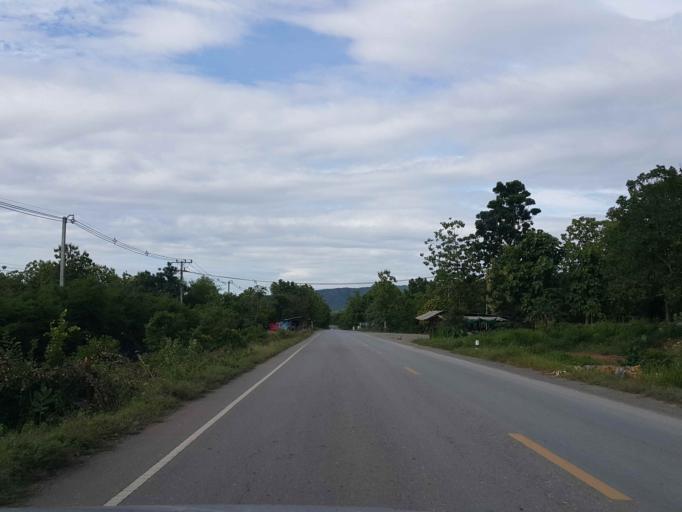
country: TH
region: Sukhothai
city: Thung Saliam
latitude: 17.2504
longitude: 99.5194
